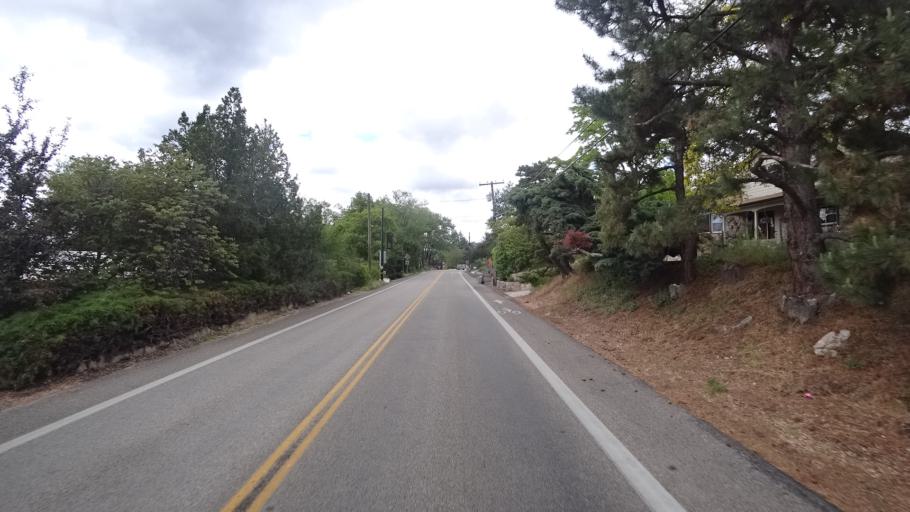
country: US
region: Idaho
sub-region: Ada County
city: Garden City
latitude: 43.6688
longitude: -116.2536
